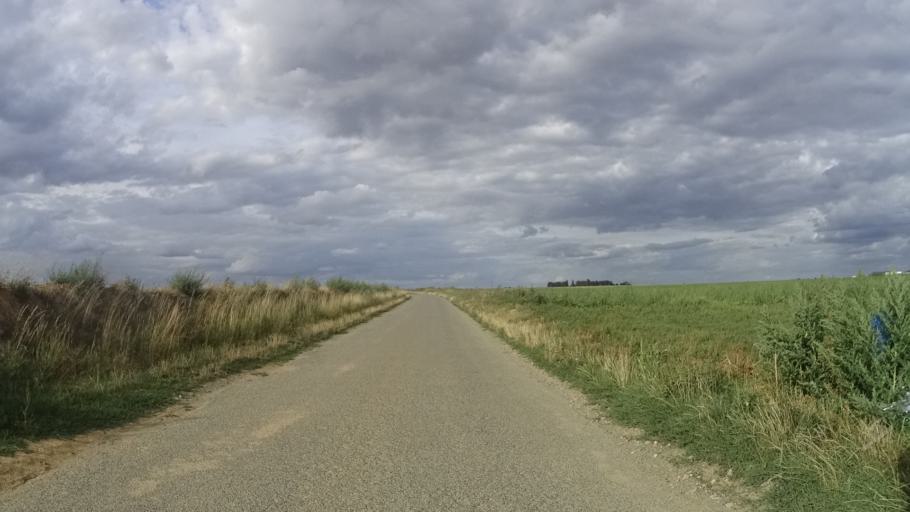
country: FR
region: Picardie
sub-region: Departement de l'Oise
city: Ver-sur-Launette
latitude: 49.0982
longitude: 2.7139
